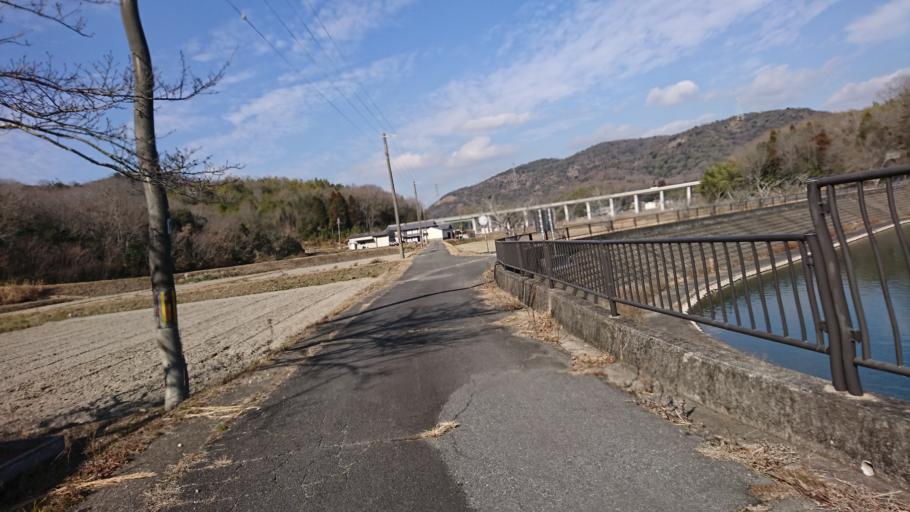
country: JP
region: Hyogo
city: Ono
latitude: 34.8344
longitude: 134.8658
